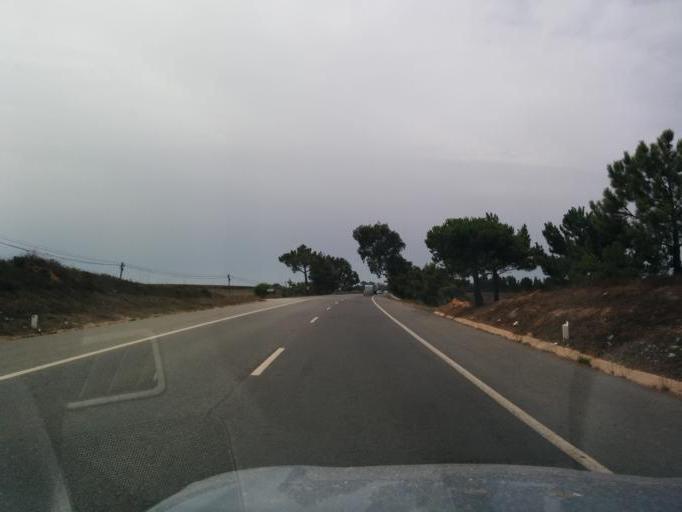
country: PT
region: Beja
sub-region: Odemira
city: Vila Nova de Milfontes
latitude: 37.7169
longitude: -8.7665
